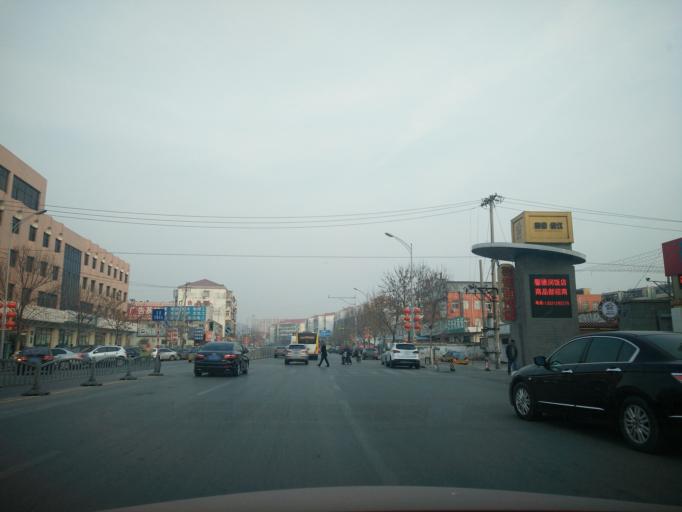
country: CN
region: Beijing
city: Jiugong
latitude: 39.8034
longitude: 116.4337
